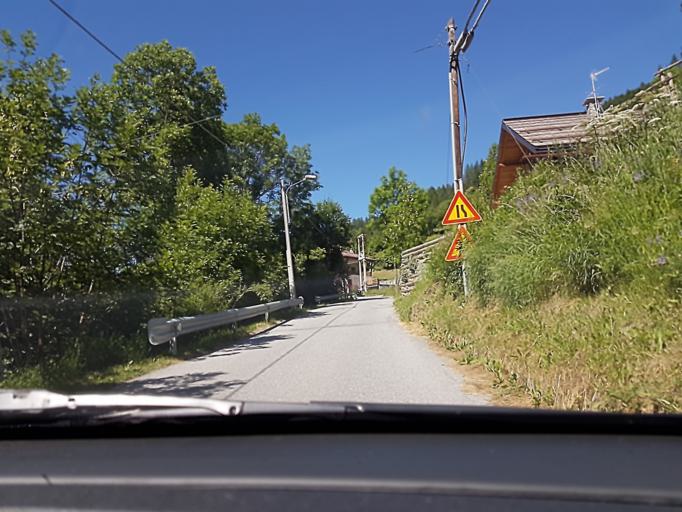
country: IT
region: Piedmont
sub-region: Provincia di Torino
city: Cesana Torinese
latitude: 44.9674
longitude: 6.7998
